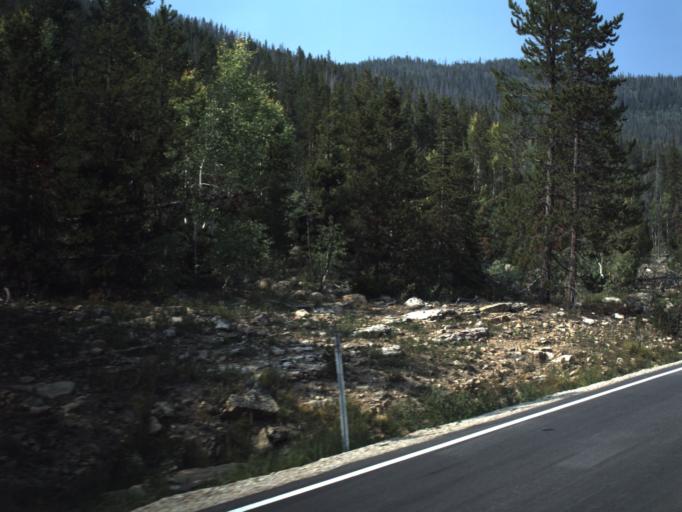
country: US
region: Utah
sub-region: Summit County
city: Francis
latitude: 40.6256
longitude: -110.9608
